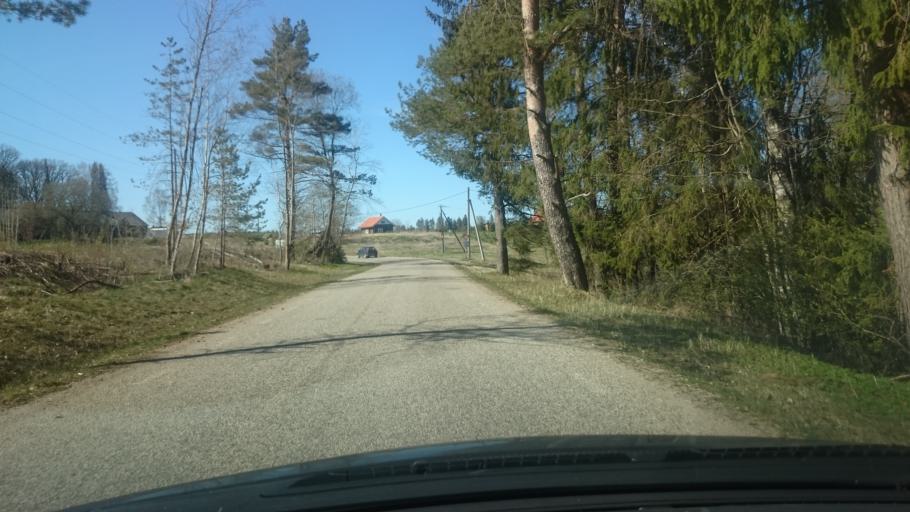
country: EE
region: Polvamaa
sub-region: Polva linn
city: Polva
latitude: 58.1344
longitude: 27.0166
